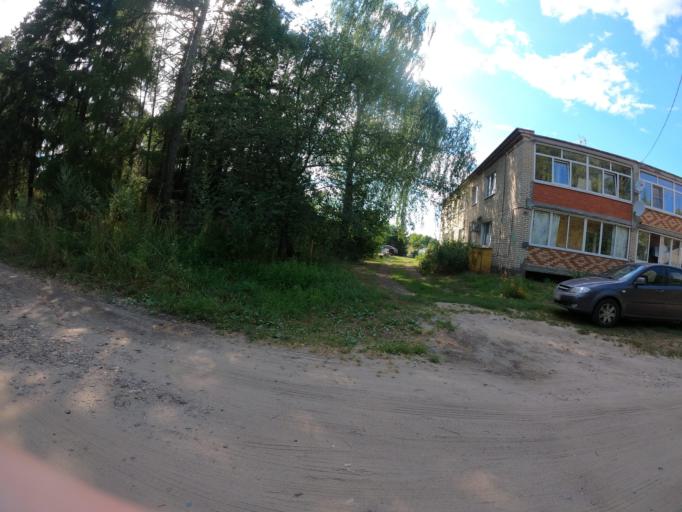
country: RU
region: Moskovskaya
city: Konobeyevo
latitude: 55.3921
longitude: 38.7082
